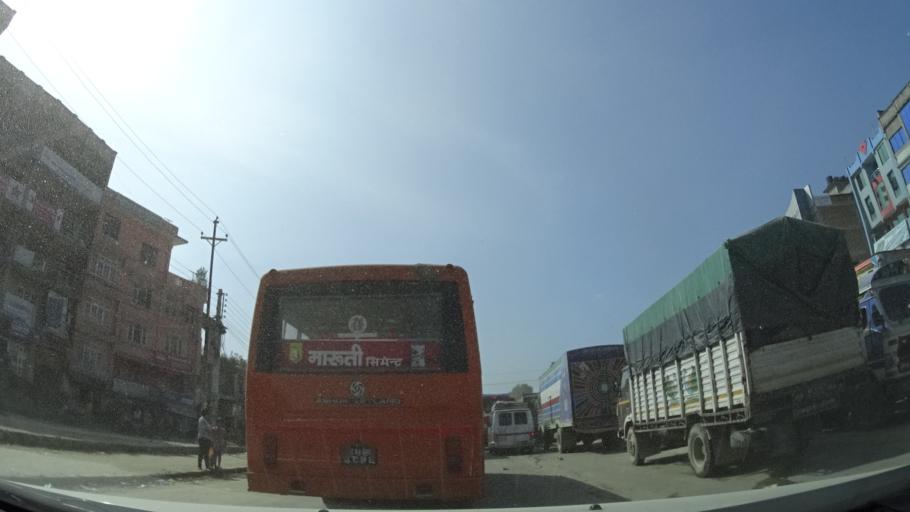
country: NP
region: Central Region
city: Kirtipur
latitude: 27.6970
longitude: 85.2817
